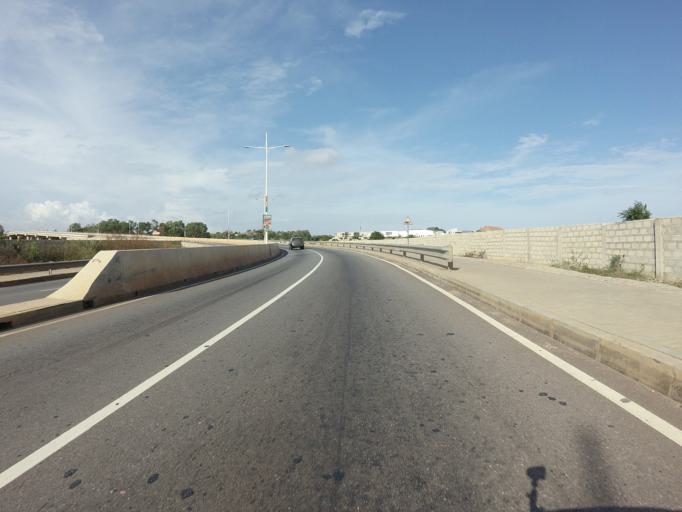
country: GH
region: Greater Accra
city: Medina Estates
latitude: 5.6169
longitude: -0.1534
